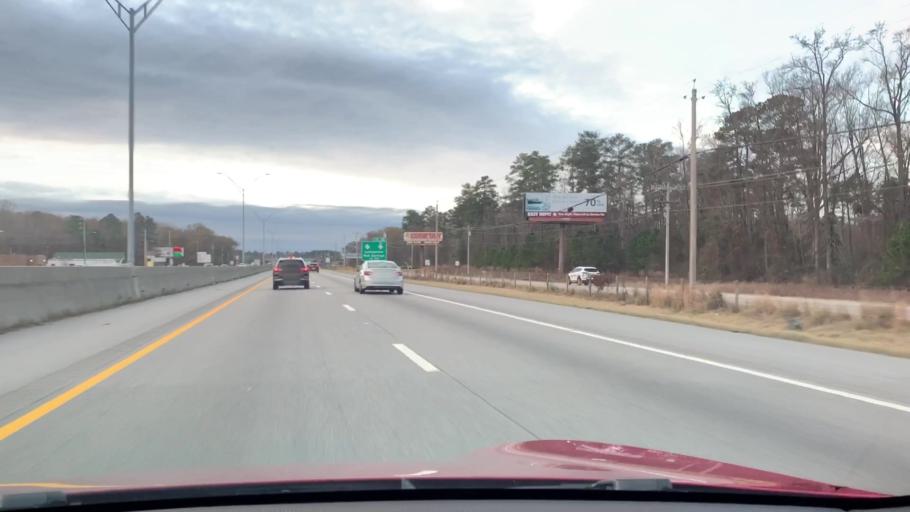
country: US
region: North Carolina
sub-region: Robeson County
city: Lumberton
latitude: 34.6563
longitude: -79.0105
